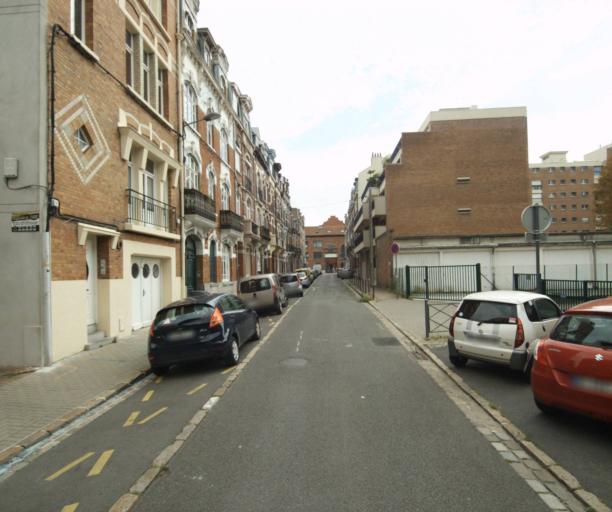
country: FR
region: Nord-Pas-de-Calais
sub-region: Departement du Nord
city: Lille
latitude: 50.6266
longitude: 3.0451
